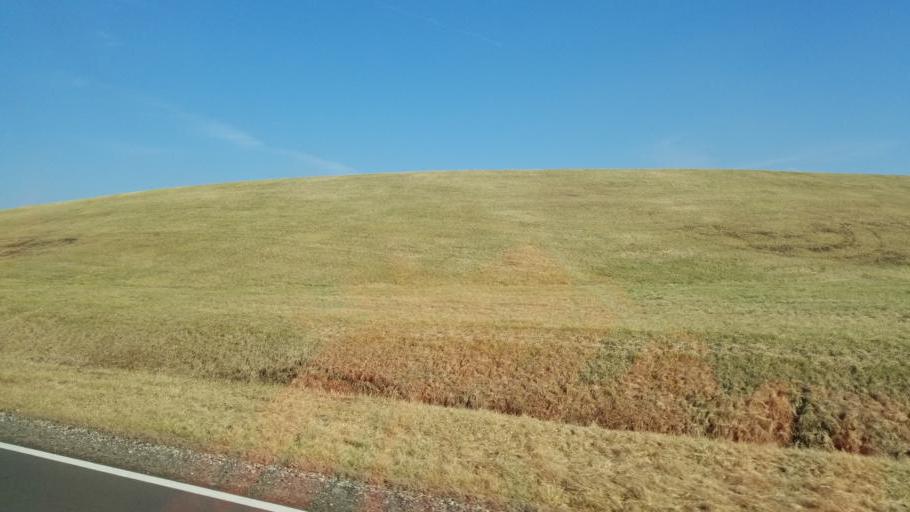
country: US
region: Ohio
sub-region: Crawford County
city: Bucyrus
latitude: 40.8375
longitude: -82.9402
